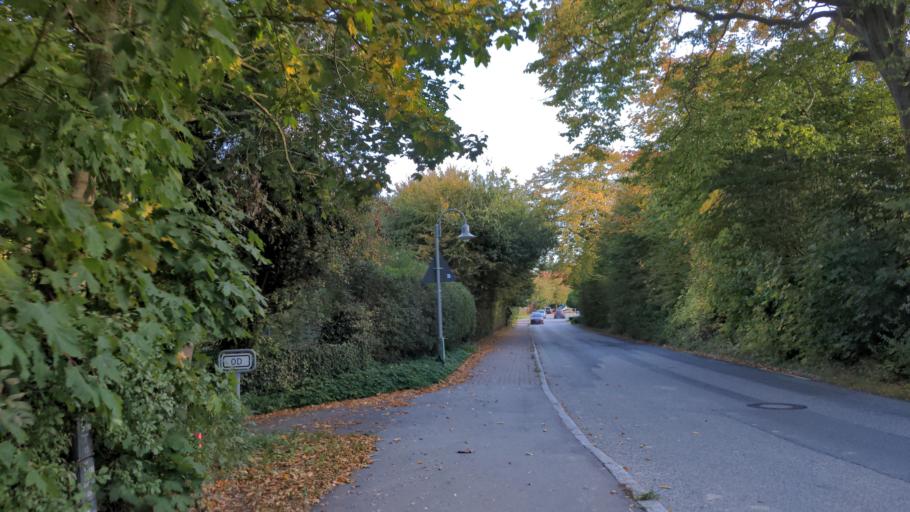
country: DE
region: Schleswig-Holstein
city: Manhagen
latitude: 54.1985
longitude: 10.9120
